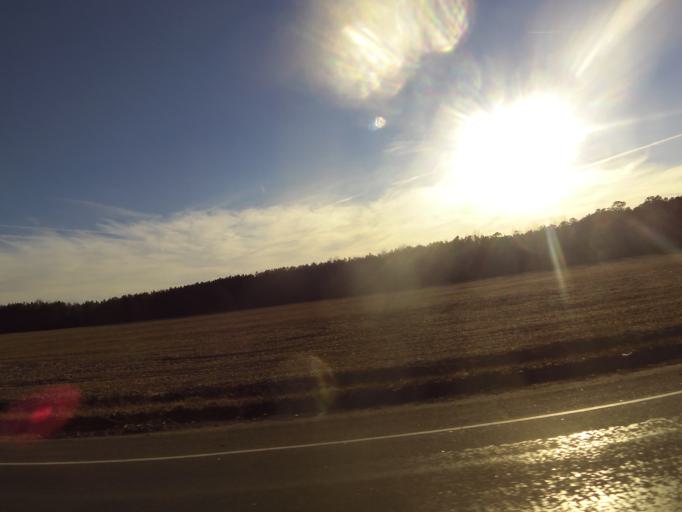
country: US
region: Virginia
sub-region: City of Franklin
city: Franklin
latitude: 36.6699
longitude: -76.8904
